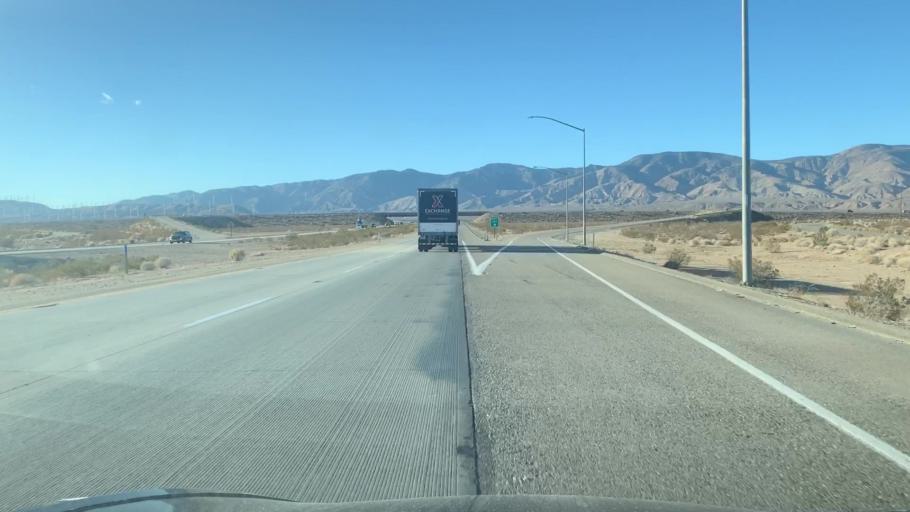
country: US
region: California
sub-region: Kern County
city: Mojave
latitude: 35.0960
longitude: -118.1378
